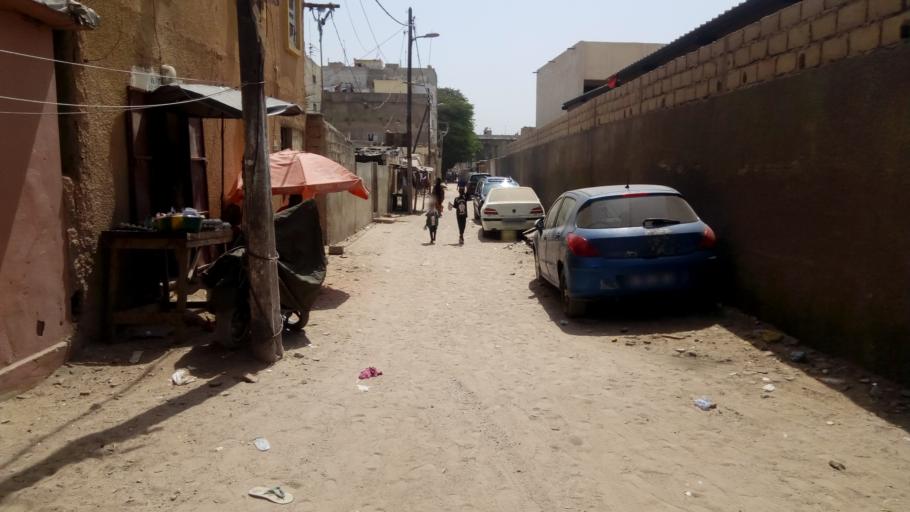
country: SN
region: Dakar
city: Grand Dakar
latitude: 14.7136
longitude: -17.4478
